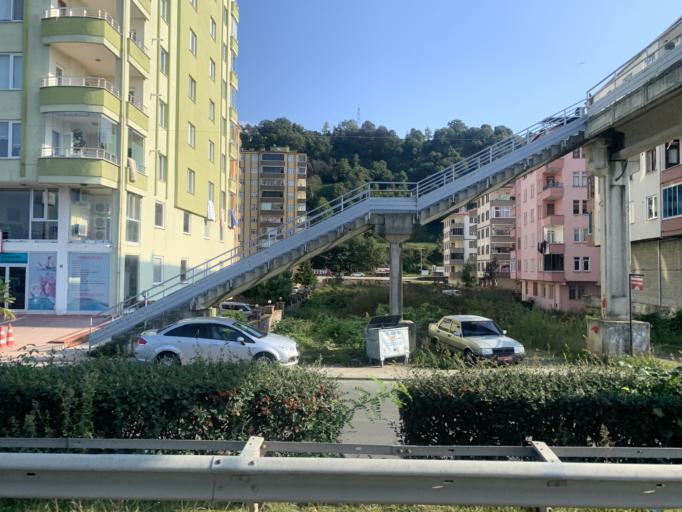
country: TR
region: Trabzon
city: Of
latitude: 40.9420
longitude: 40.2593
